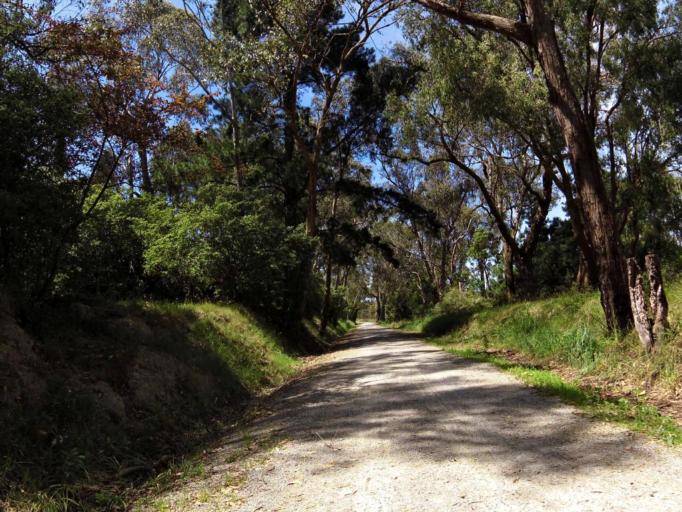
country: AU
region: Victoria
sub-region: Yarra Ranges
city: Lilydale
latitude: -37.7615
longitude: 145.3628
